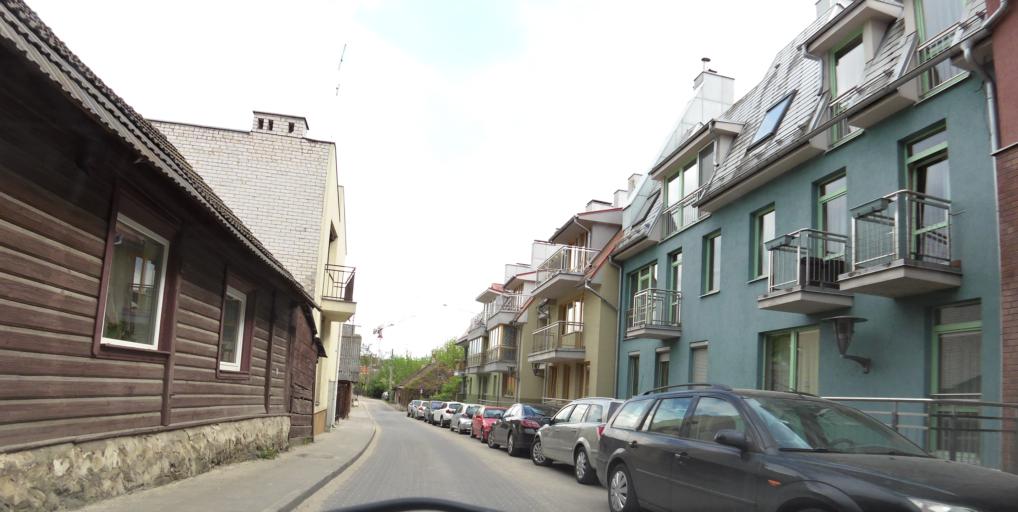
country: LT
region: Vilnius County
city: Rasos
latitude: 54.6823
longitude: 25.3014
